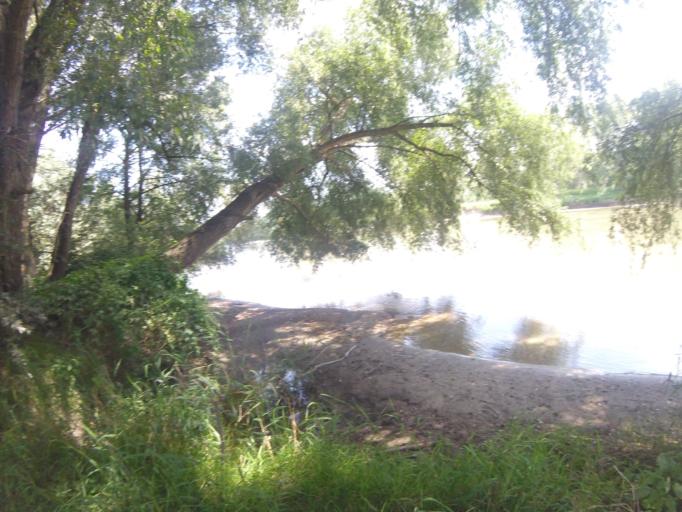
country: HU
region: Zala
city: Murakeresztur
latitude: 46.3545
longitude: 16.8610
